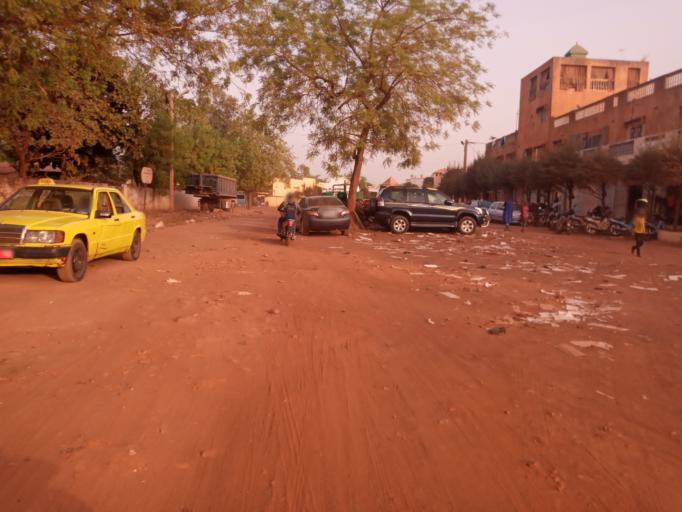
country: ML
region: Bamako
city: Bamako
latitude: 12.5931
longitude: -7.9592
